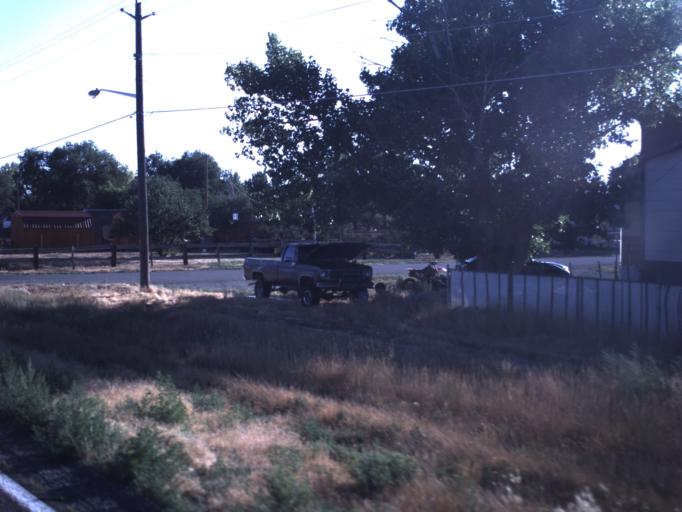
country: US
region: Utah
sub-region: Iron County
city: Enoch
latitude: 37.7577
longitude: -113.0552
